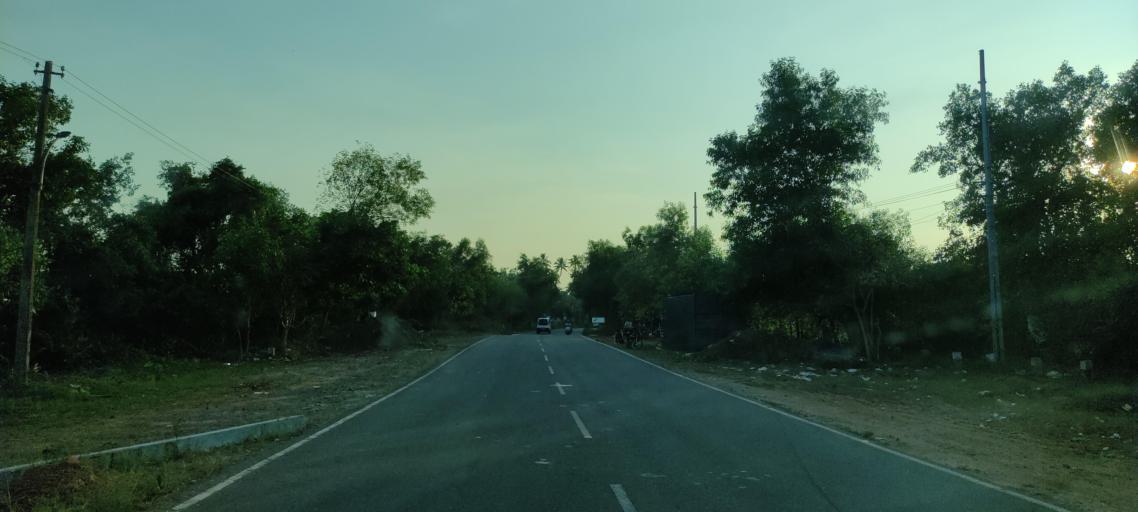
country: IN
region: Kerala
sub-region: Alappuzha
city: Kutiatodu
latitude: 9.7741
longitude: 76.3310
